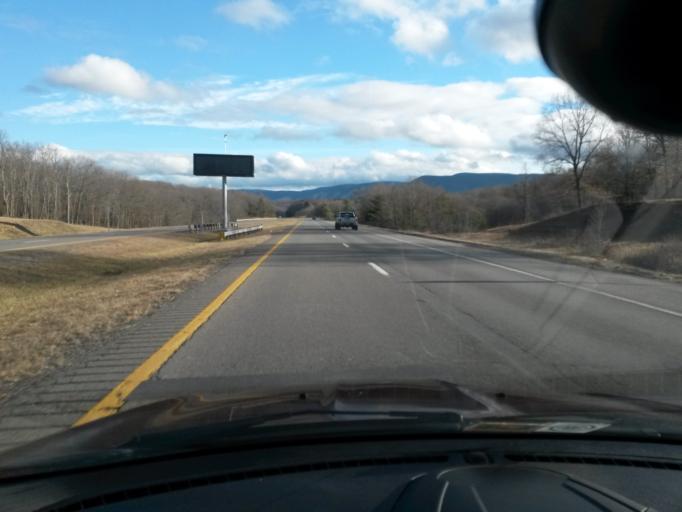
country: US
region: West Virginia
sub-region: Mercer County
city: Athens
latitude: 37.3612
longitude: -81.0290
